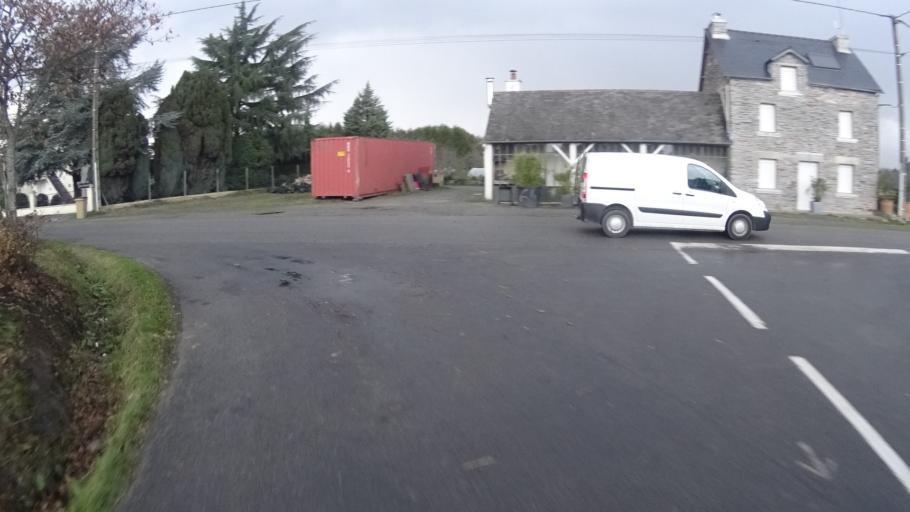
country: FR
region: Brittany
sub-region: Departement d'Ille-et-Vilaine
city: Sainte-Marie
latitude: 47.6767
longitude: -2.0353
